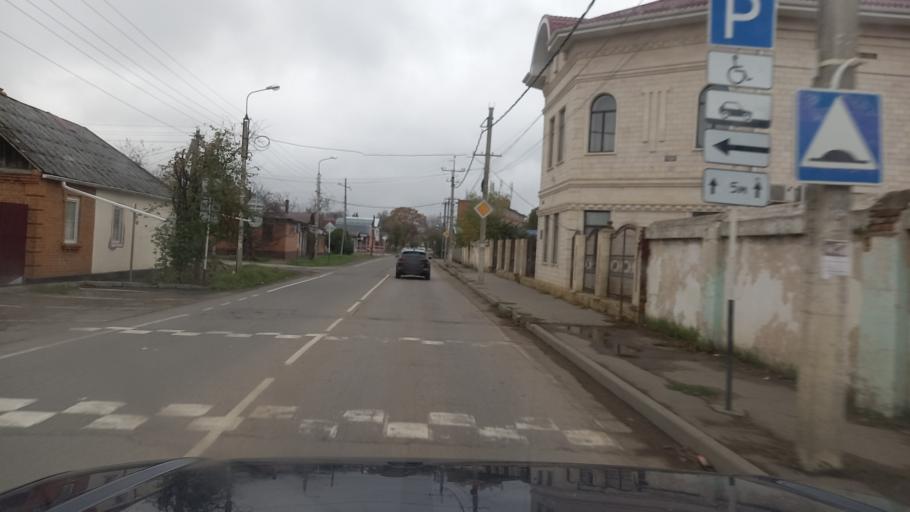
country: RU
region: Adygeya
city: Maykop
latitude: 44.6066
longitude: 40.0918
